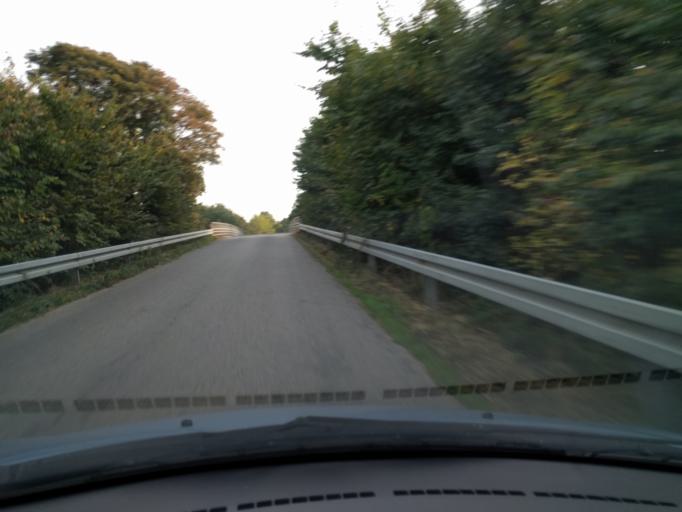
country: DK
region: South Denmark
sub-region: Kerteminde Kommune
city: Langeskov
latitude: 55.3798
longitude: 10.5207
